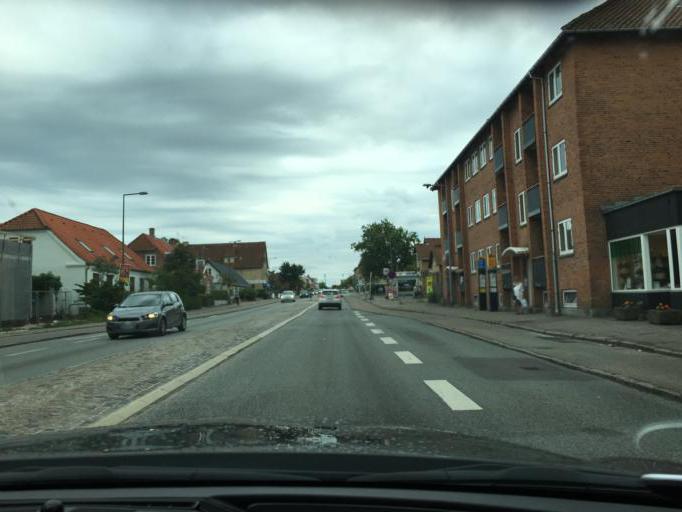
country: DK
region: Capital Region
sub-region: Horsholm Kommune
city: Horsholm
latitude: 55.8865
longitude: 12.4973
